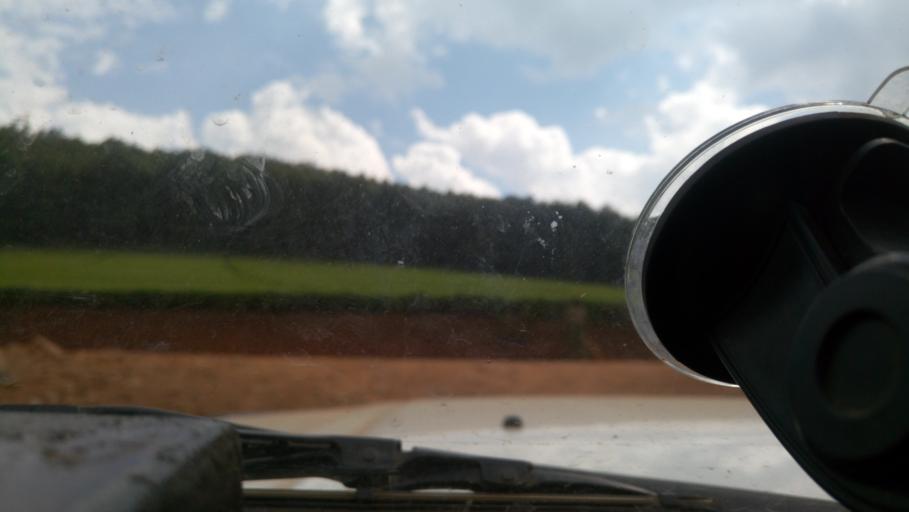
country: KE
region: Kericho
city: Sotik
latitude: -0.6037
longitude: 35.0628
